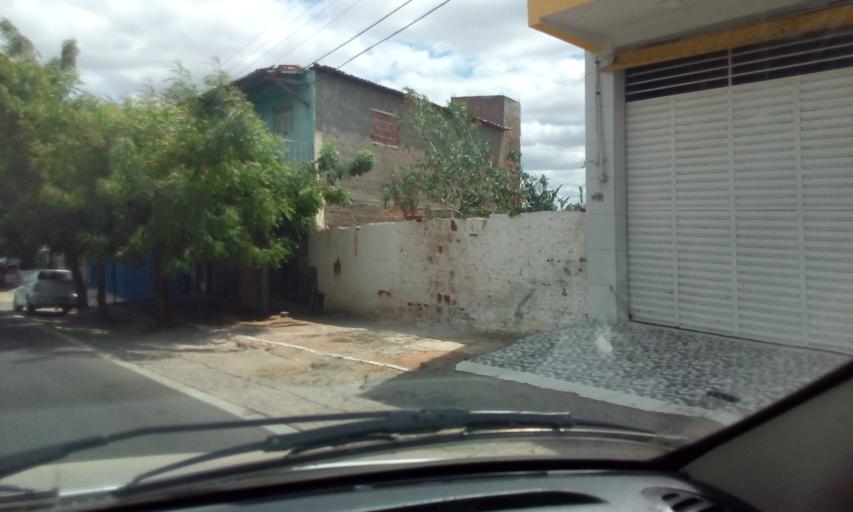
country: BR
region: Rio Grande do Norte
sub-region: Currais Novos
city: Currais Novos
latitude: -6.2595
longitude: -36.5143
